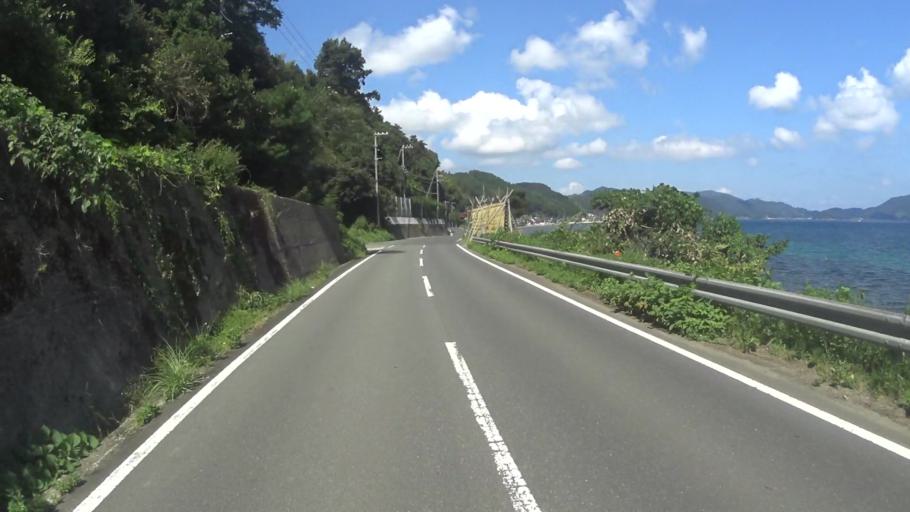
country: JP
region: Kyoto
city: Miyazu
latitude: 35.6432
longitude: 135.2507
